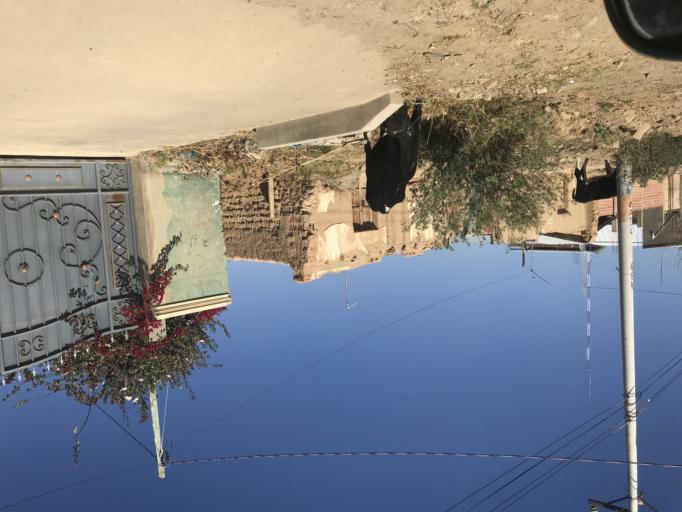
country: BO
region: Cochabamba
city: Cliza
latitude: -17.5941
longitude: -65.9442
